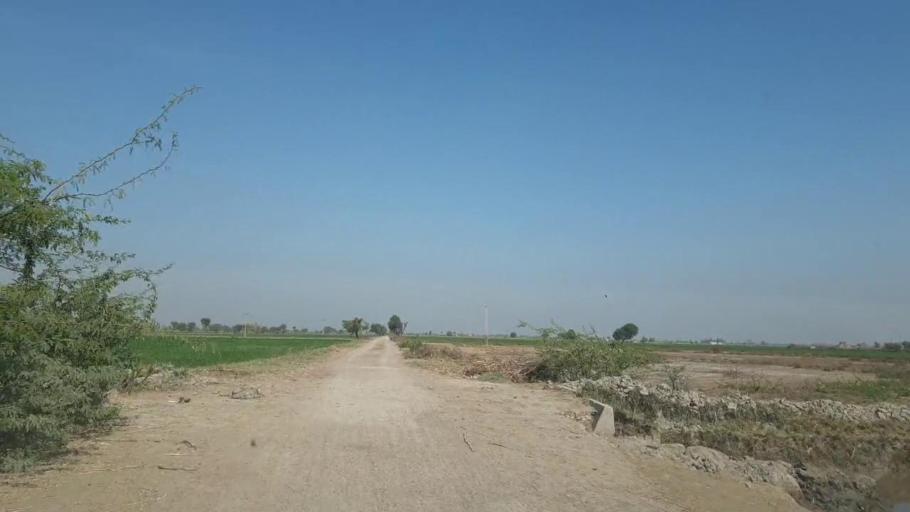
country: PK
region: Sindh
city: Mirpur Khas
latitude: 25.5598
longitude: 69.1837
